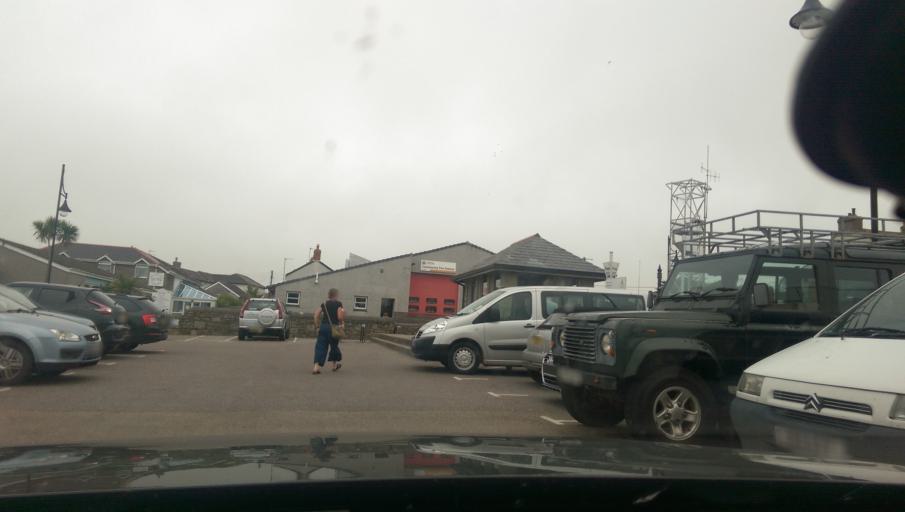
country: GB
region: England
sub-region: Cornwall
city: Saint Just
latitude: 50.1235
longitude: -5.6815
